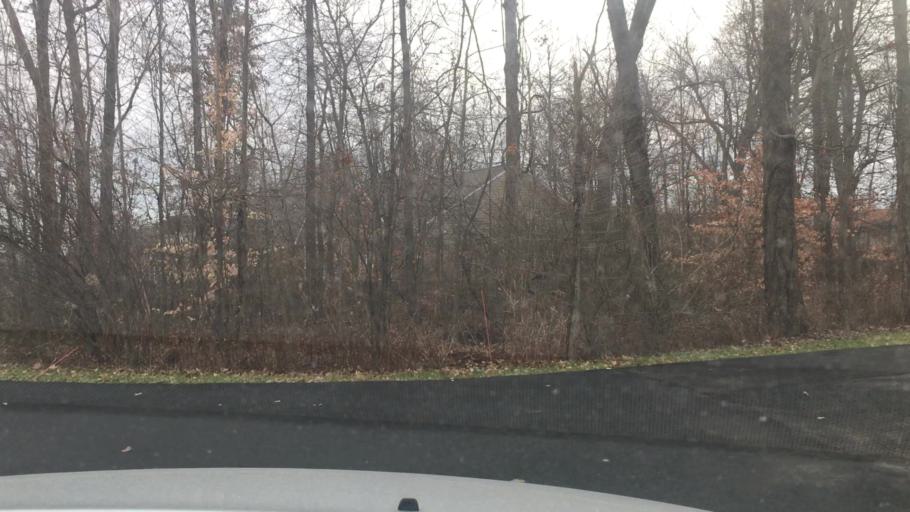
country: US
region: Ohio
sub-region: Franklin County
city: Westerville
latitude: 40.1422
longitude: -82.9098
